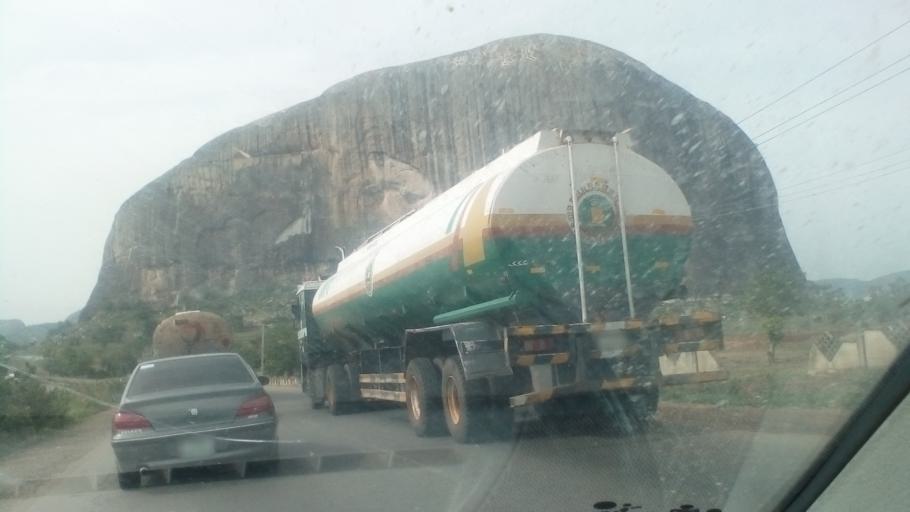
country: NG
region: Abuja Federal Capital Territory
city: Madala
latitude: 9.1224
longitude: 7.2284
